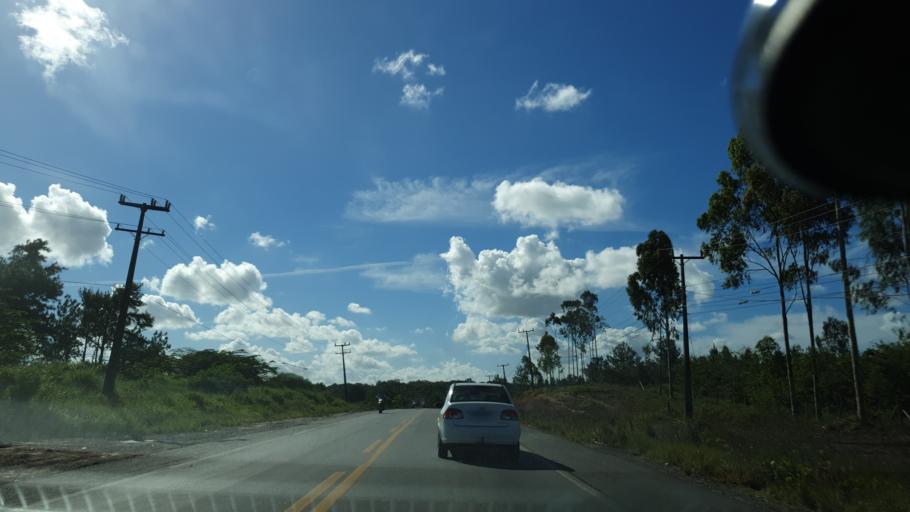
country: BR
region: Bahia
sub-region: Camacari
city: Camacari
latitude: -12.6840
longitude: -38.2779
